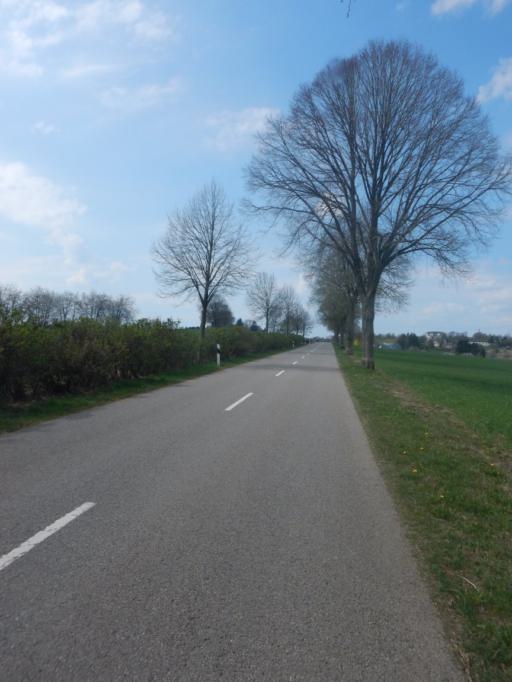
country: LU
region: Diekirch
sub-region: Canton de Clervaux
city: Clervaux
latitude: 50.0582
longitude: 6.0110
